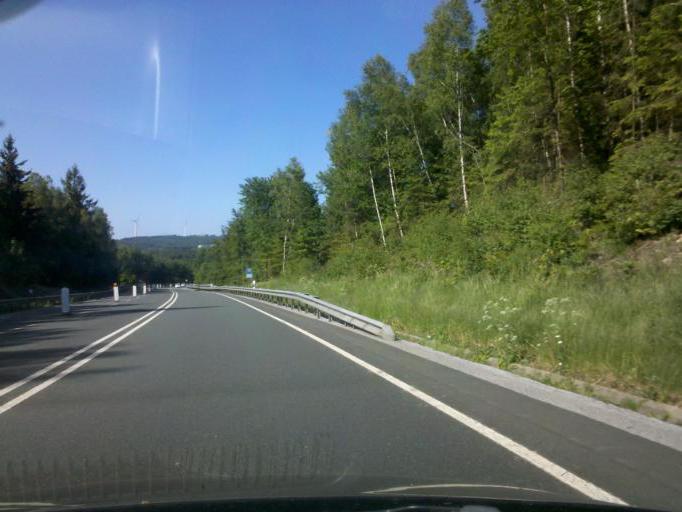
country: DE
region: Hesse
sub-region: Regierungsbezirk Giessen
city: Haiger
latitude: 50.7541
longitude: 8.1466
